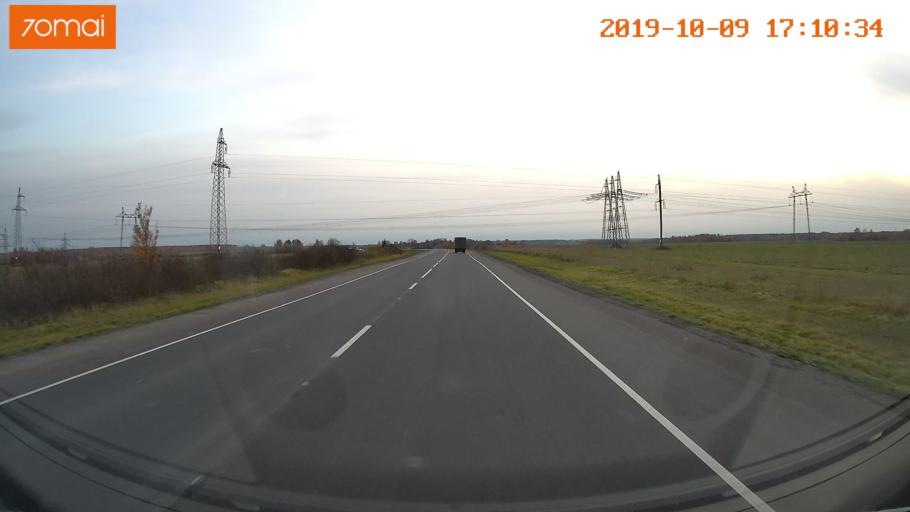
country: RU
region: Ivanovo
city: Privolzhsk
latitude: 57.3540
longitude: 41.2575
